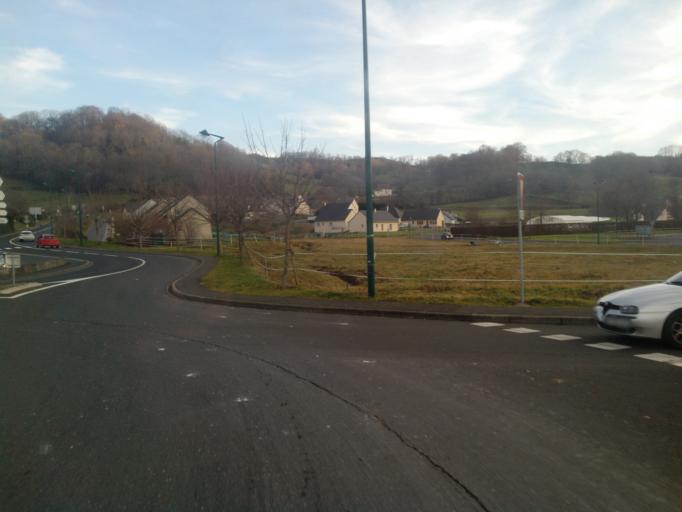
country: FR
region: Auvergne
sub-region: Departement du Cantal
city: Riom-es-Montagnes
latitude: 45.2798
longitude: 2.6641
